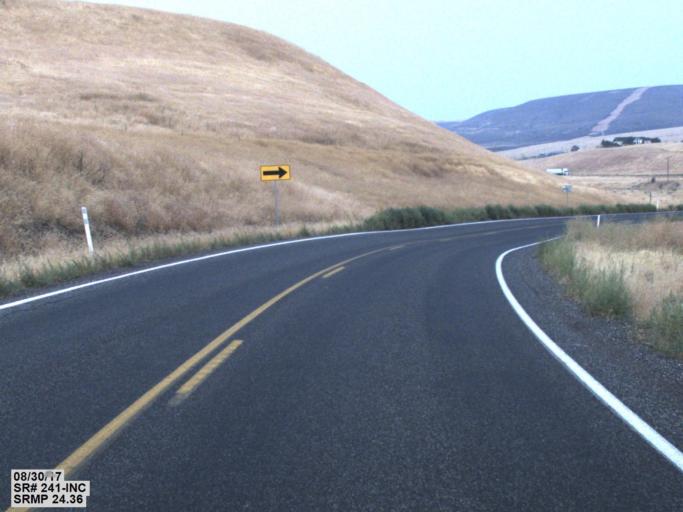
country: US
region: Washington
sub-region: Grant County
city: Desert Aire
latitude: 46.5233
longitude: -119.8742
